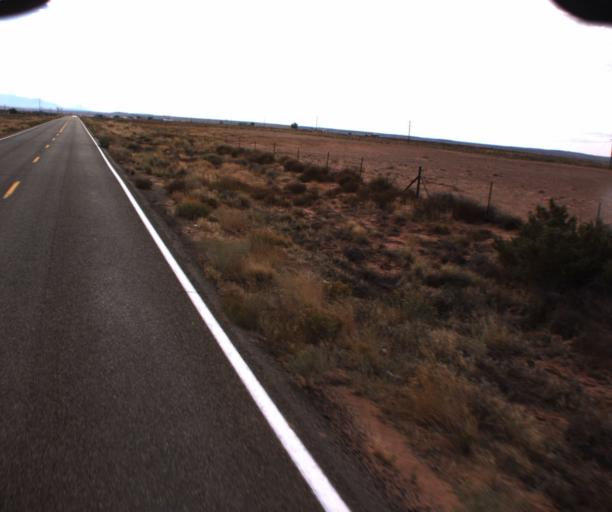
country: US
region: Arizona
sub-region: Apache County
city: Many Farms
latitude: 36.5196
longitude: -109.4895
